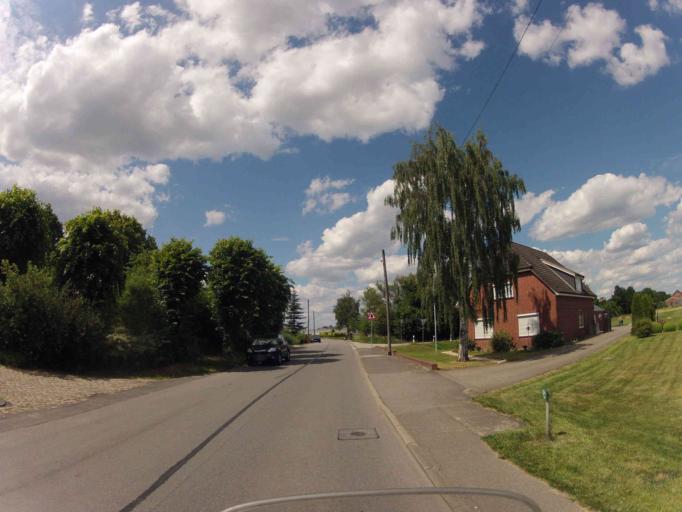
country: DE
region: Hamburg
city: Bergedorf
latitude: 53.4248
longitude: 10.2009
